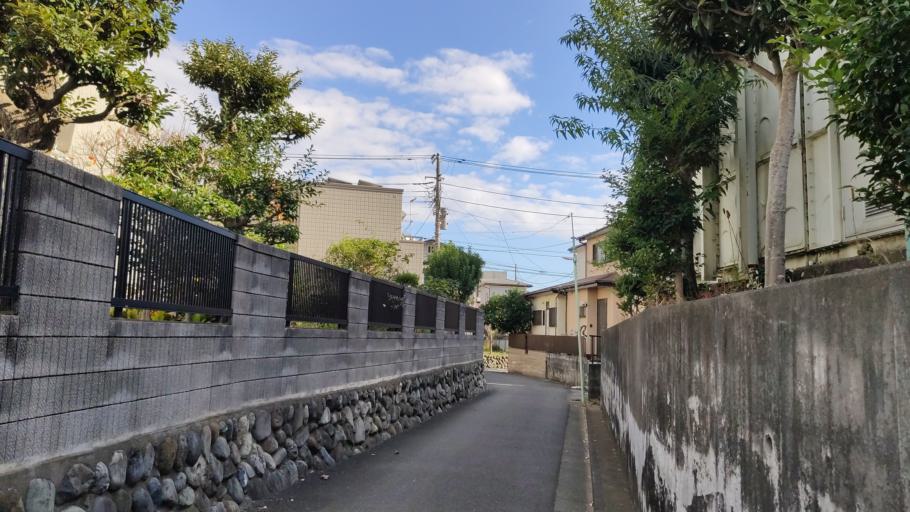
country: JP
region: Kanagawa
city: Fujisawa
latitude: 35.3379
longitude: 139.4960
